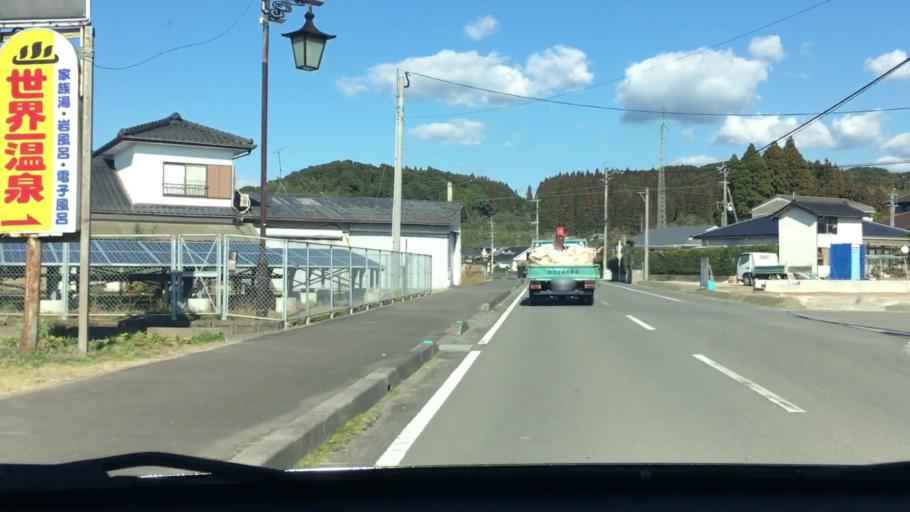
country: JP
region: Kagoshima
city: Satsumasendai
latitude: 31.7919
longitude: 130.4095
